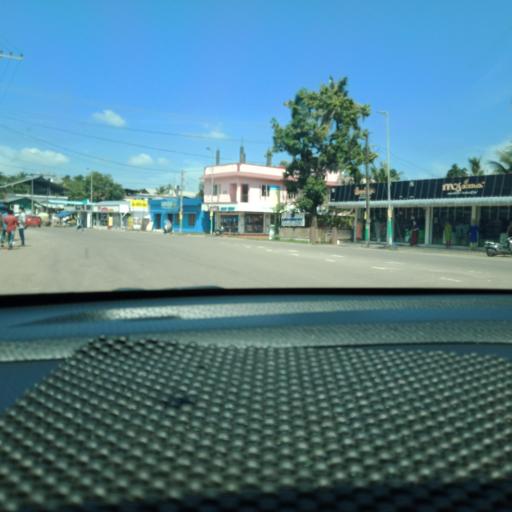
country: IN
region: Kerala
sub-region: Alappuzha
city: Mavelikara
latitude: 9.2818
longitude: 76.4542
